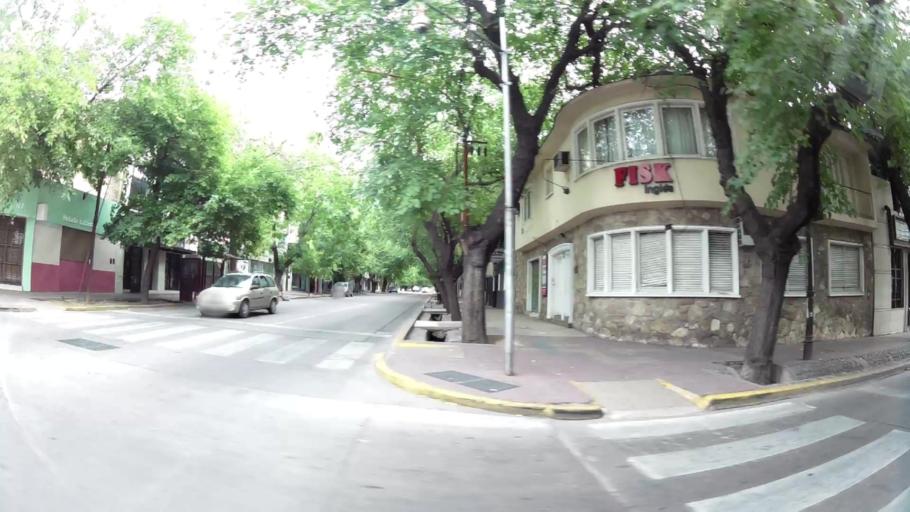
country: AR
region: Mendoza
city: Mendoza
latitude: -32.8931
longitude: -68.8441
